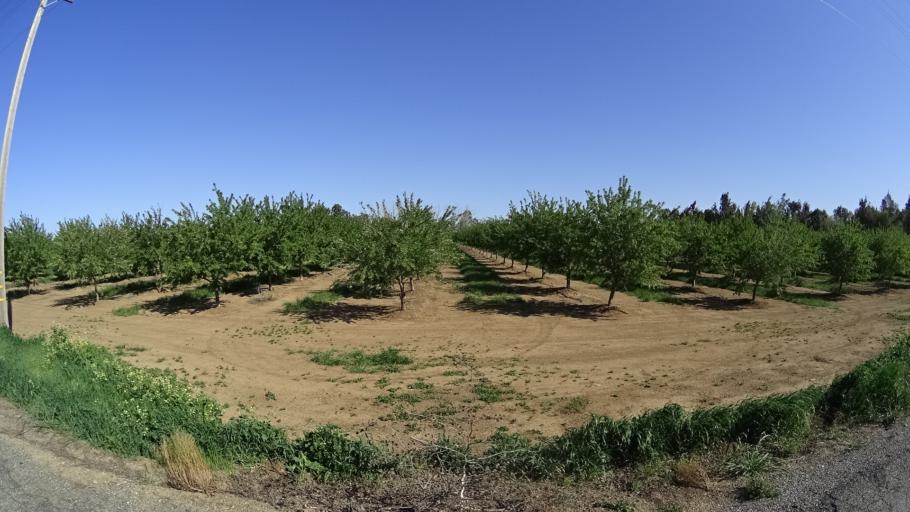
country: US
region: California
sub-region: Glenn County
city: Hamilton City
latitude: 39.7757
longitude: -122.0936
